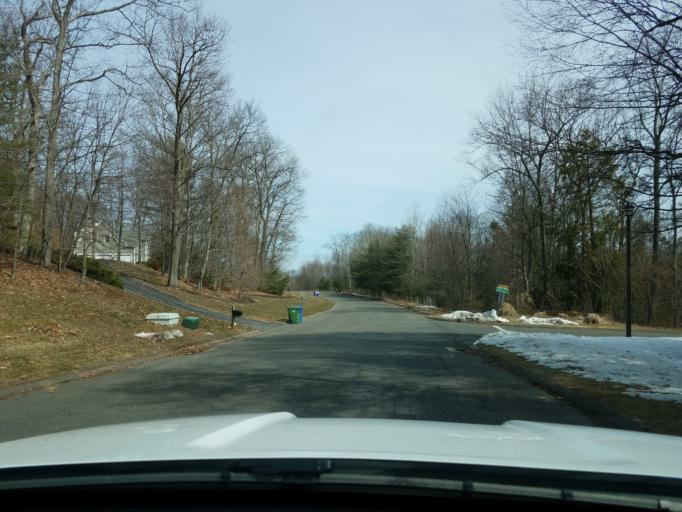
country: US
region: Connecticut
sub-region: Hartford County
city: Collinsville
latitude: 41.8053
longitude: -72.9124
